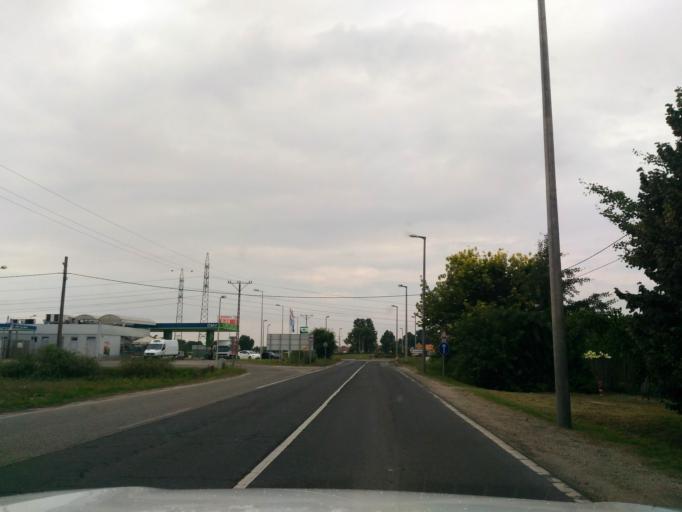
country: HU
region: Pest
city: Alsonemedi
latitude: 47.3013
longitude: 19.1808
